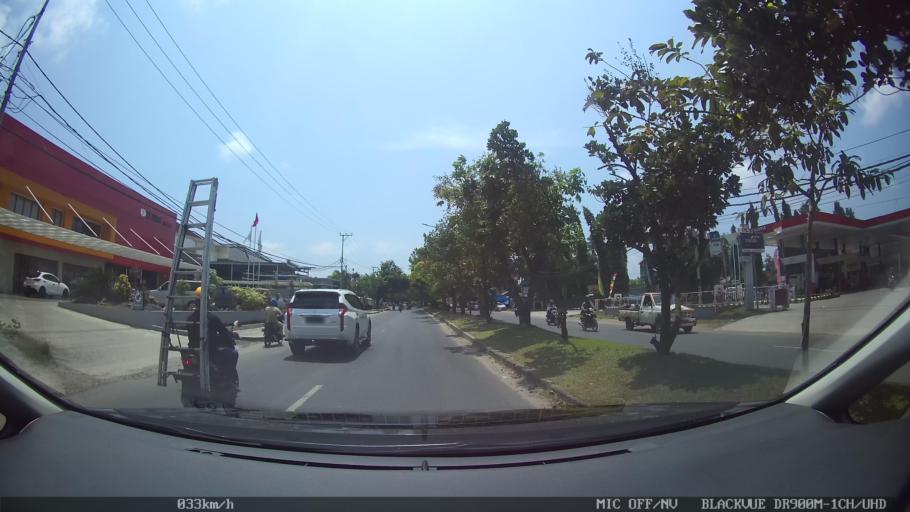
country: ID
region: Lampung
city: Kedaton
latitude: -5.3811
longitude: 105.2692
